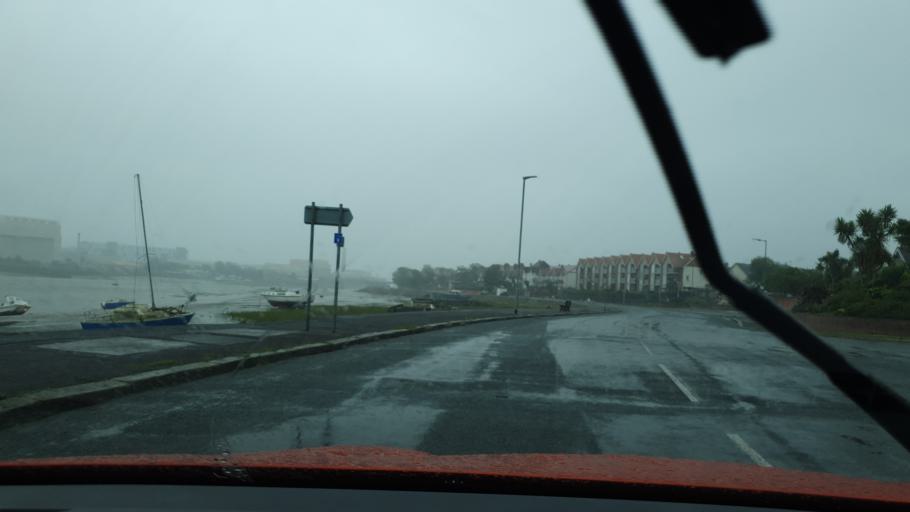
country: GB
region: England
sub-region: Cumbria
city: Barrow in Furness
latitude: 54.1148
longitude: -3.2504
